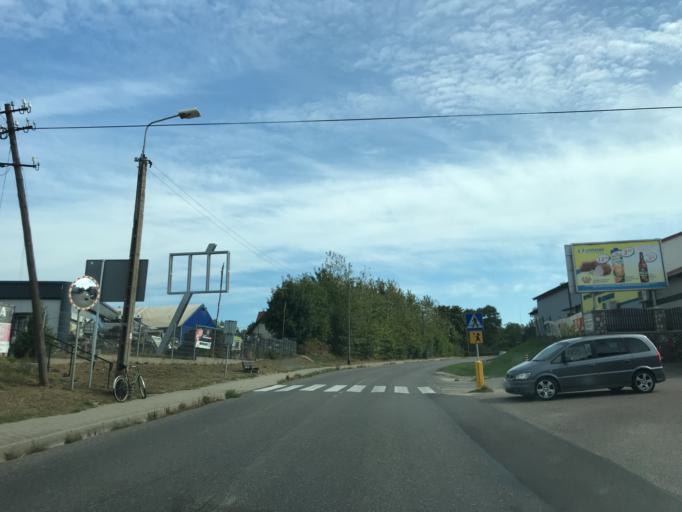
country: PL
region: Pomeranian Voivodeship
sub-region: Powiat pucki
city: Krokowa
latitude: 54.7825
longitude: 18.1716
